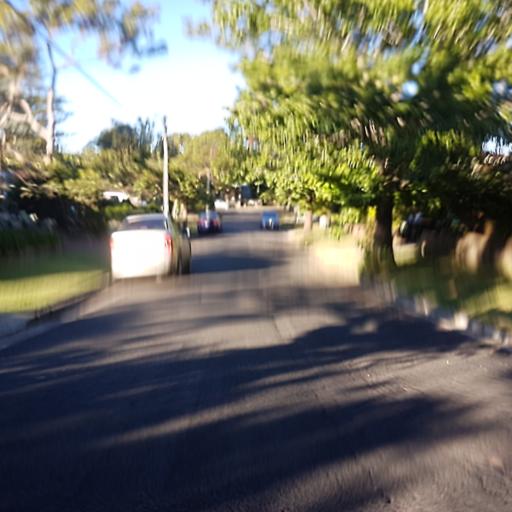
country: AU
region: New South Wales
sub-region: Warringah
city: Forestville
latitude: -33.7587
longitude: 151.2117
